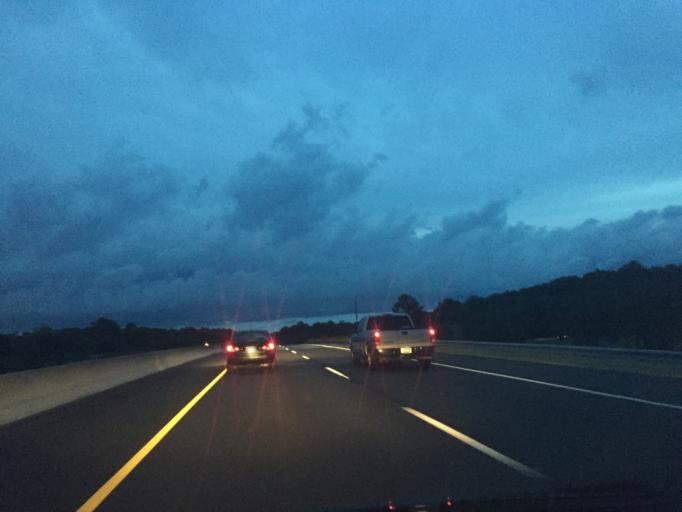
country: US
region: Georgia
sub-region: Chatham County
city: Georgetown
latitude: 32.0004
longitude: -81.2496
